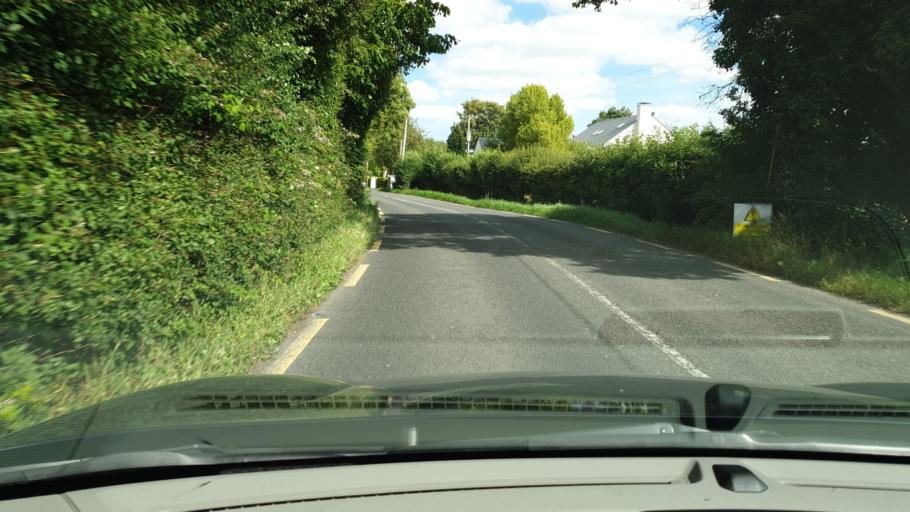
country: IE
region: Leinster
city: Lucan
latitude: 53.3727
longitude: -6.4506
